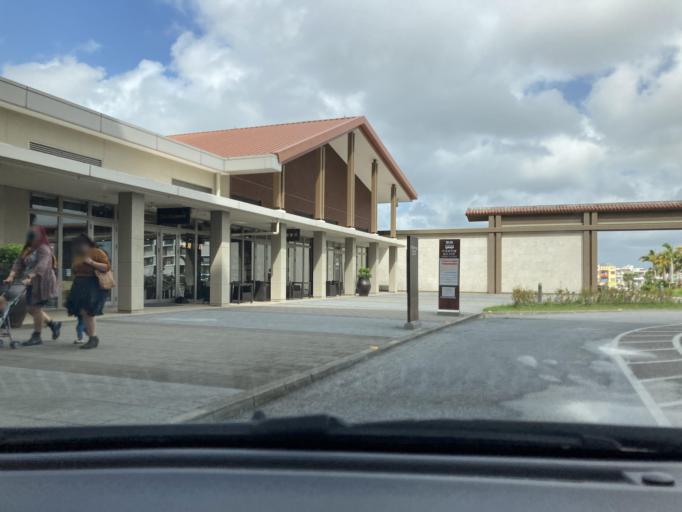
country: JP
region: Okinawa
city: Okinawa
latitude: 26.3147
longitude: 127.7964
